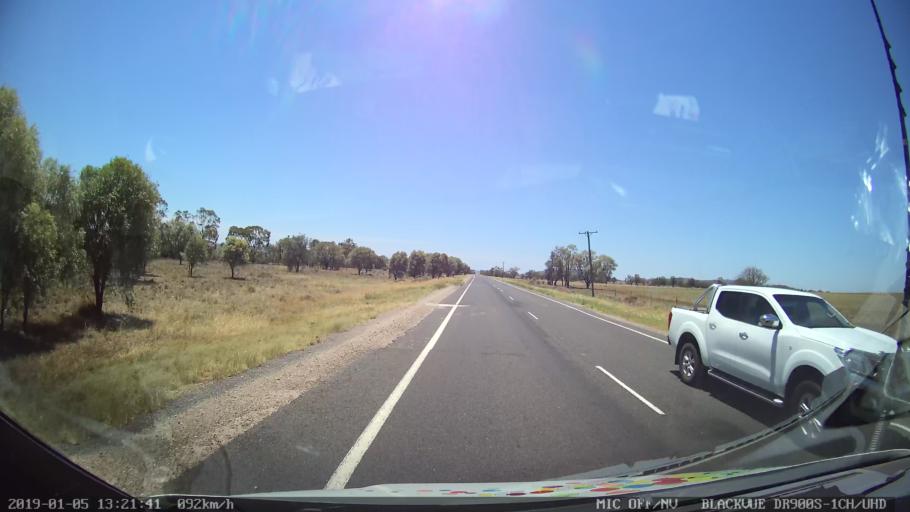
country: AU
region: New South Wales
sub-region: Gunnedah
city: Gunnedah
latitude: -31.0923
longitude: 149.9520
